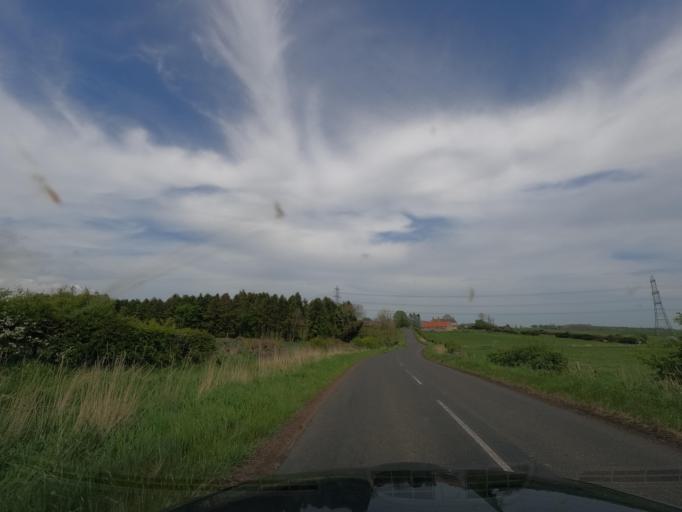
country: GB
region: England
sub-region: Northumberland
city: Whittingham
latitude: 55.4058
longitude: -1.8925
